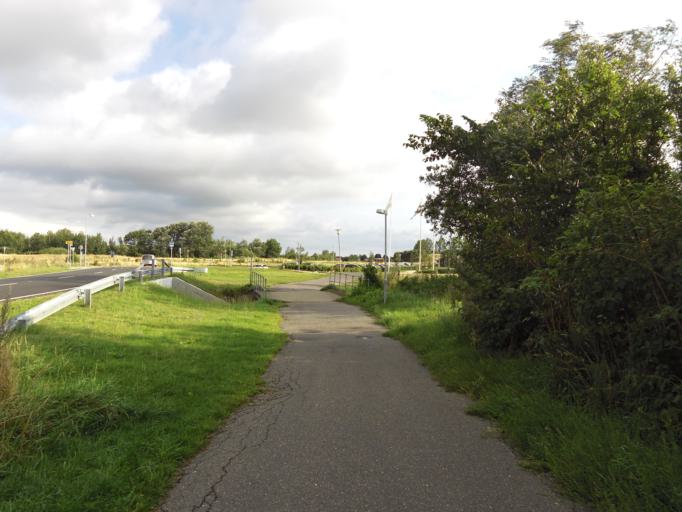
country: DK
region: South Denmark
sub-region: Esbjerg Kommune
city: Ribe
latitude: 55.3314
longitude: 8.7788
